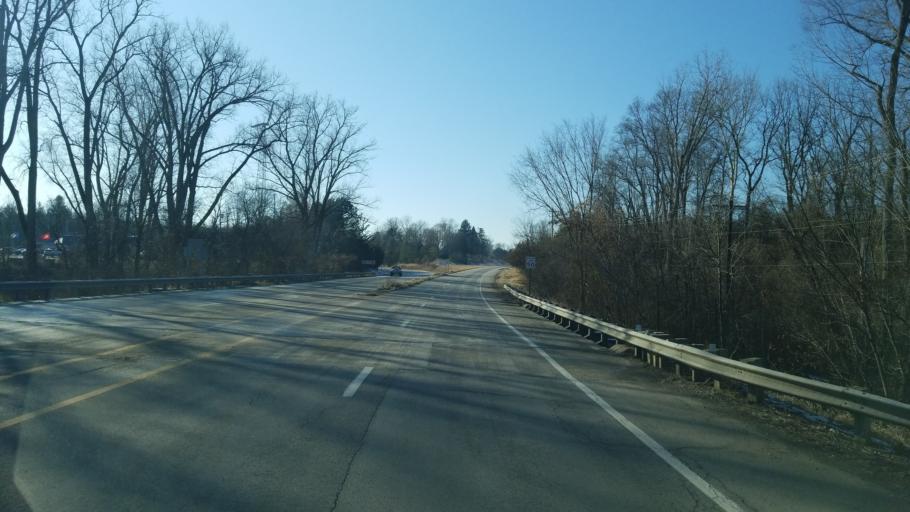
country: US
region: Ohio
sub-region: Huron County
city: Norwalk
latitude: 41.2308
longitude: -82.6448
